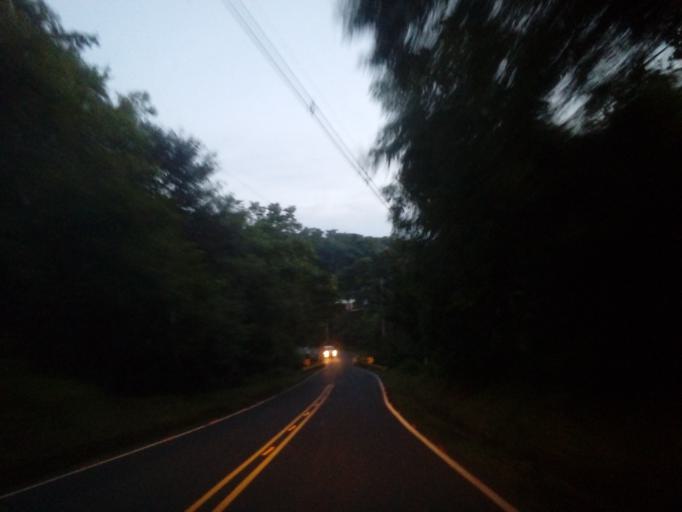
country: CR
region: Guanacaste
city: Samara
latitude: 9.9445
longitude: -85.5202
